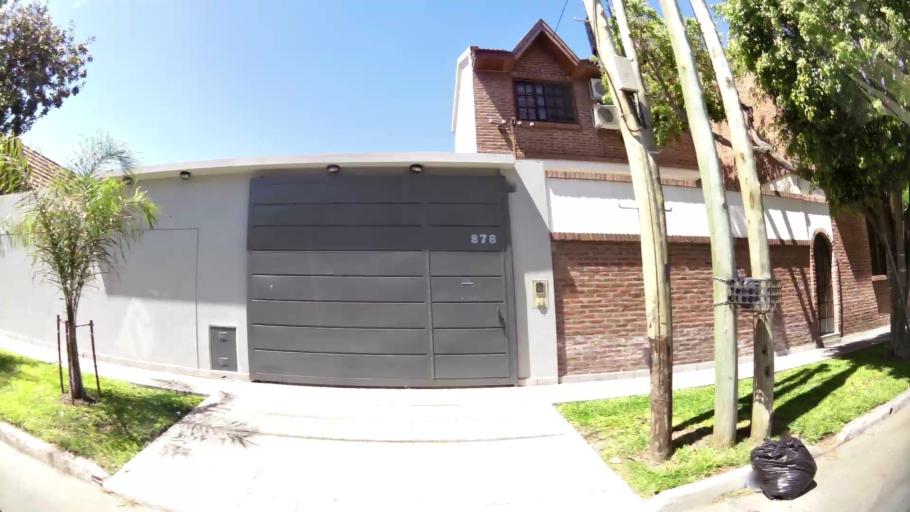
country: AR
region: Buenos Aires
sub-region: Partido de Quilmes
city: Quilmes
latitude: -34.7262
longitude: -58.2709
